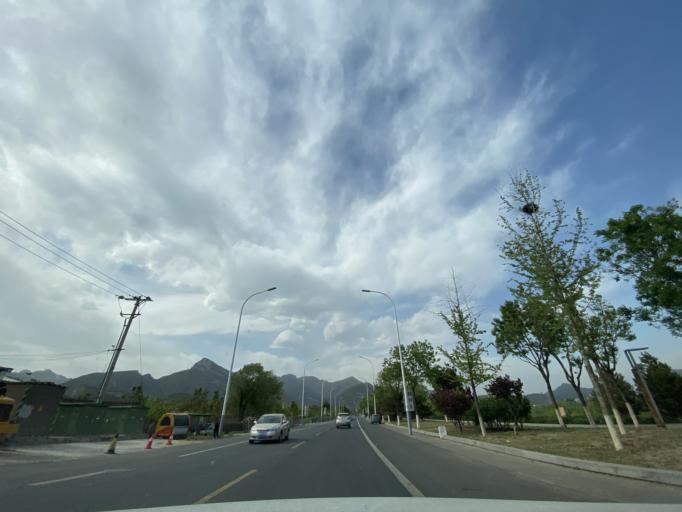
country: CN
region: Beijing
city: Junzhuang
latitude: 39.9855
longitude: 116.0809
